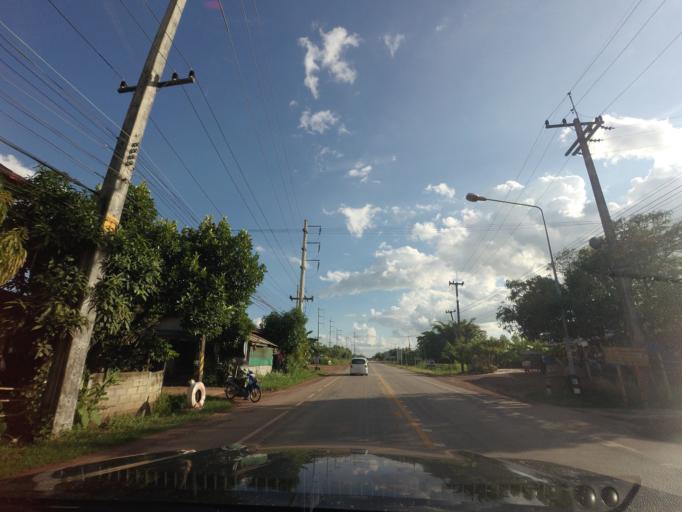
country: TH
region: Changwat Udon Thani
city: Thung Fon
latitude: 17.4876
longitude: 103.1969
